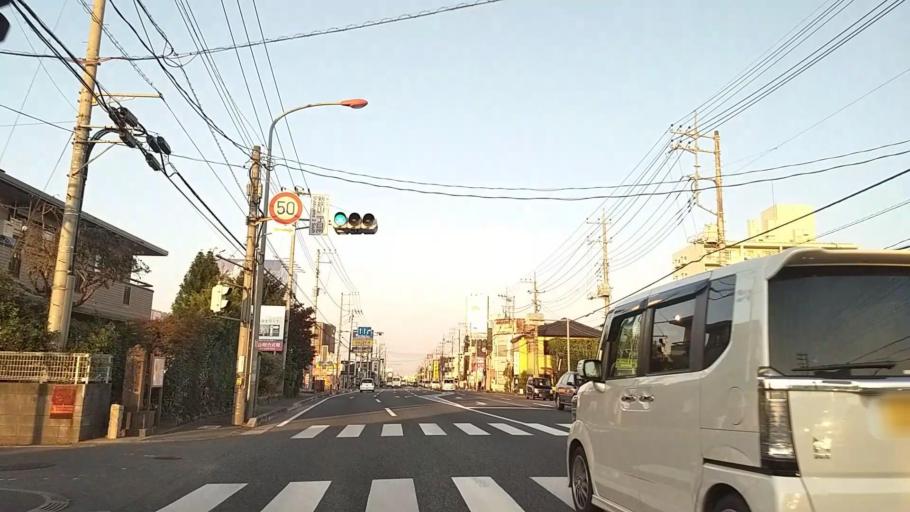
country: JP
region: Saitama
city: Sayama
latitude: 35.8758
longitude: 139.4296
